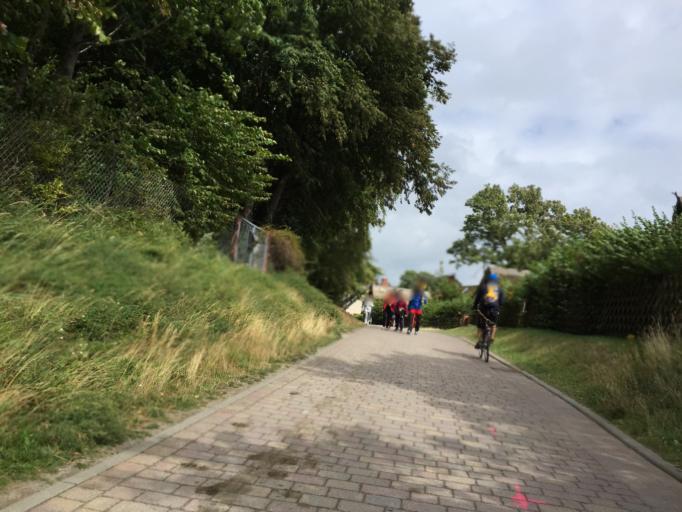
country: DE
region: Mecklenburg-Vorpommern
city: Hiddensee
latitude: 54.5846
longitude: 13.1035
